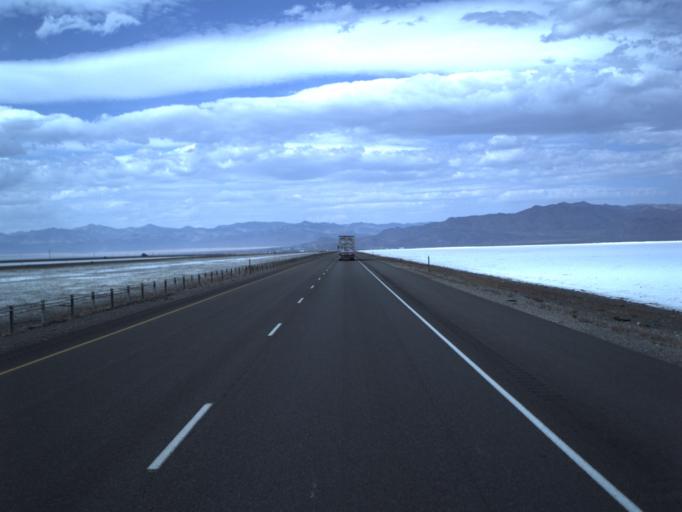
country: US
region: Utah
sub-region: Tooele County
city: Wendover
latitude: 40.7399
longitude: -113.8792
